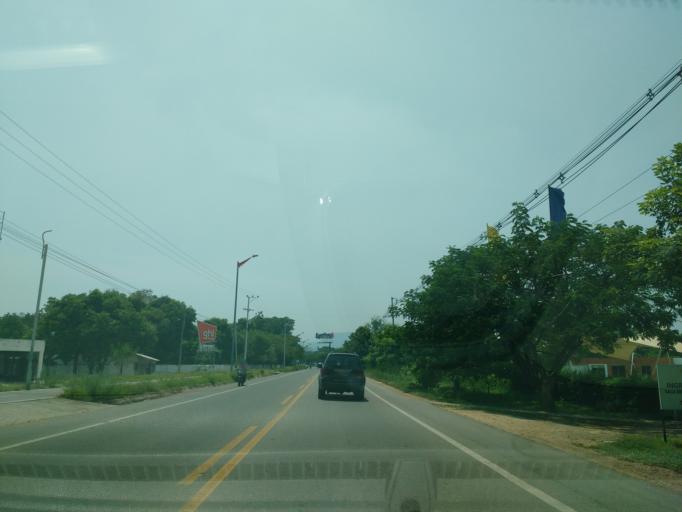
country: CO
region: Cundinamarca
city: Ricaurte
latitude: 4.2938
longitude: -74.7836
